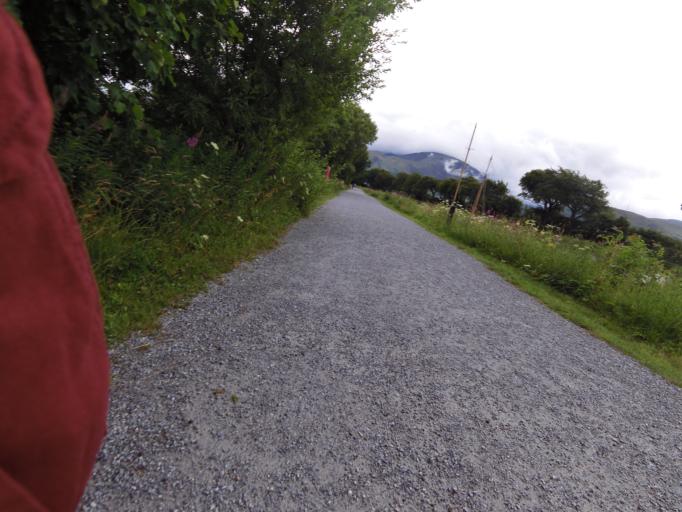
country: GB
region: Scotland
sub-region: Highland
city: Fort William
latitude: 56.8416
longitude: -5.1134
